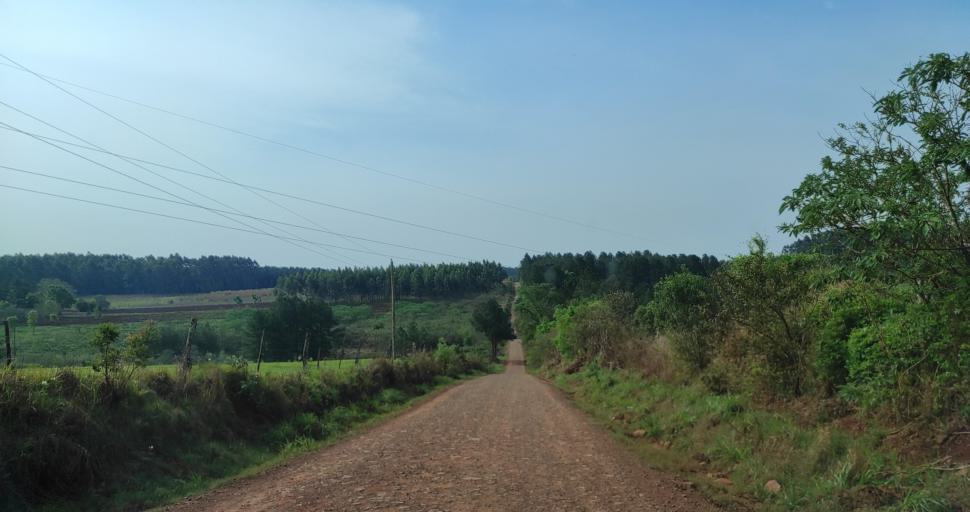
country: AR
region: Misiones
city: Garuhape
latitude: -26.8730
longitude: -55.0057
